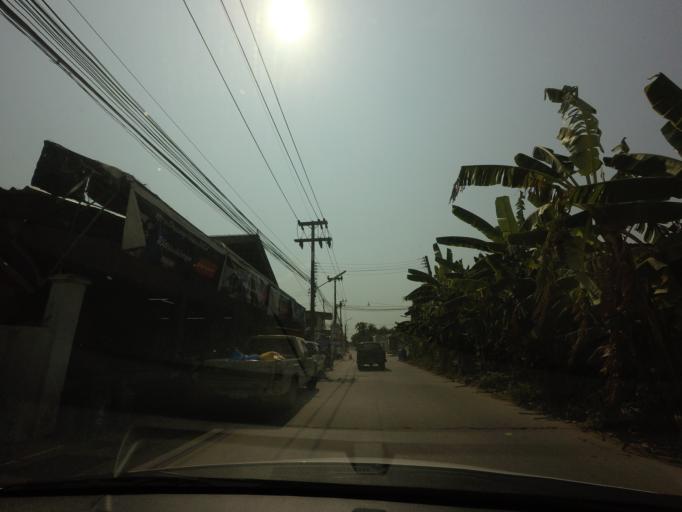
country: TH
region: Nakhon Pathom
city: Sam Phran
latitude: 13.7595
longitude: 100.2465
